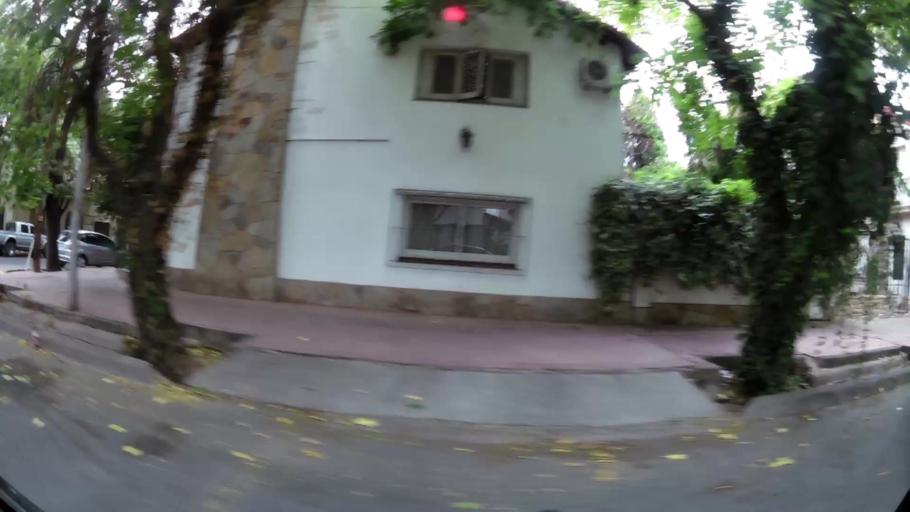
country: AR
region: Mendoza
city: Mendoza
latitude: -32.8896
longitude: -68.8529
